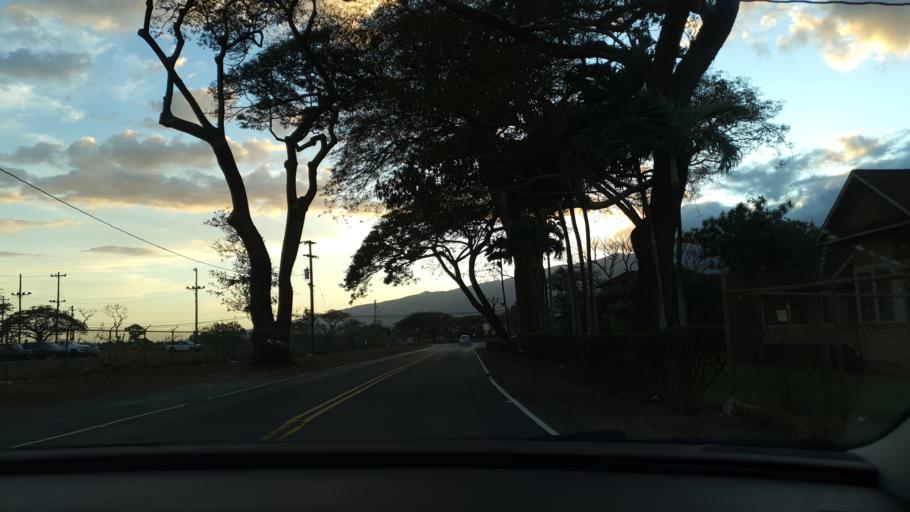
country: US
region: Hawaii
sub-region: Maui County
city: Kahului
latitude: 20.8694
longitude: -156.4544
